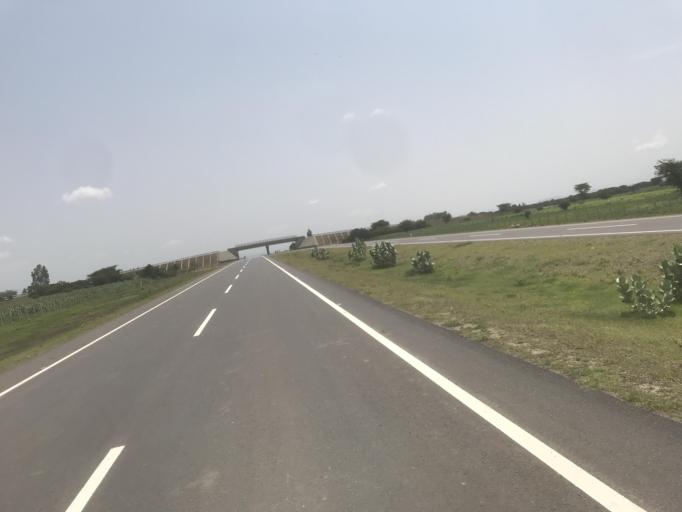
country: ET
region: Oromiya
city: Mojo
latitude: 8.2746
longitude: 38.9105
